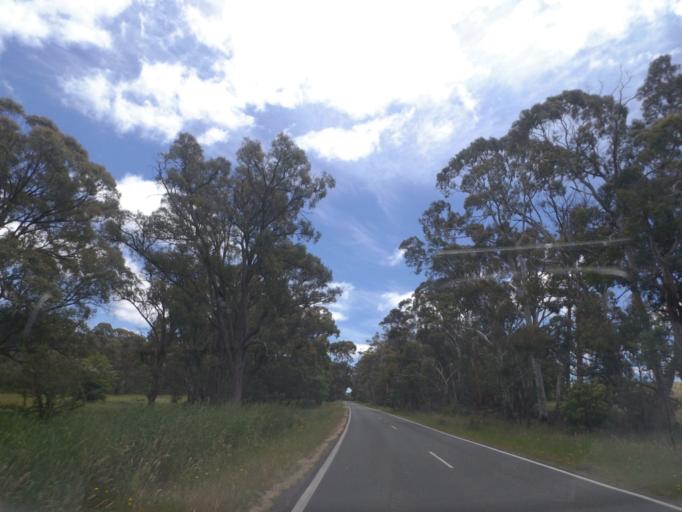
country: AU
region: Victoria
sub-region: Mount Alexander
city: Castlemaine
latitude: -37.3296
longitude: 144.1663
